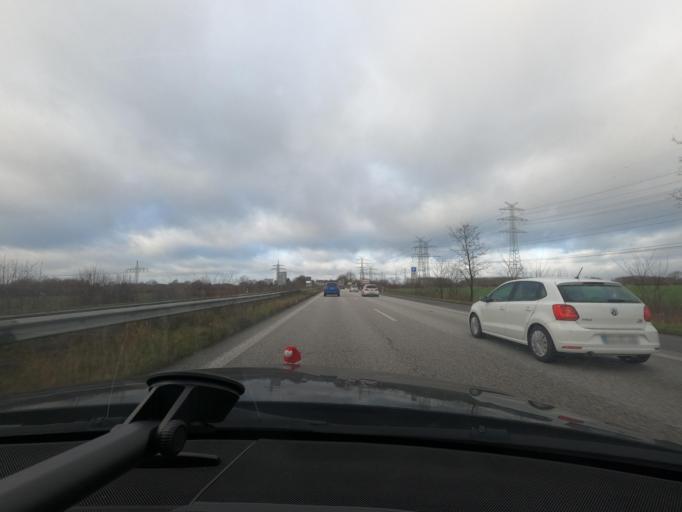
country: DE
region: Schleswig-Holstein
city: Schulldorf
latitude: 54.3156
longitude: 9.7457
